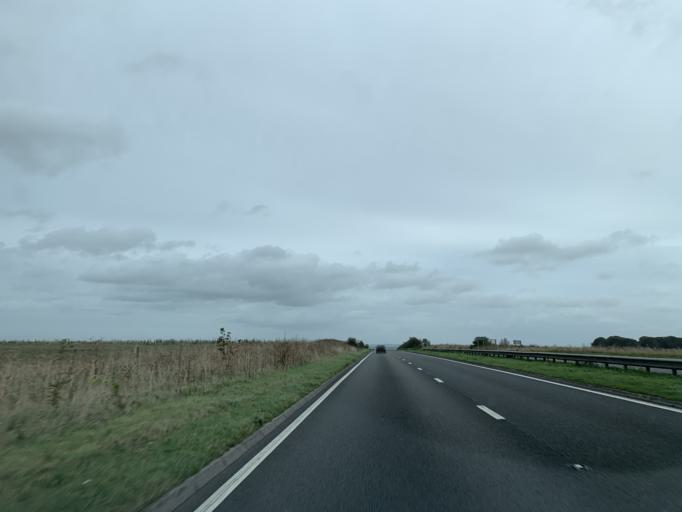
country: GB
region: England
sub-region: Wiltshire
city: Winterbourne Stoke
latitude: 51.1606
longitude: -1.9446
